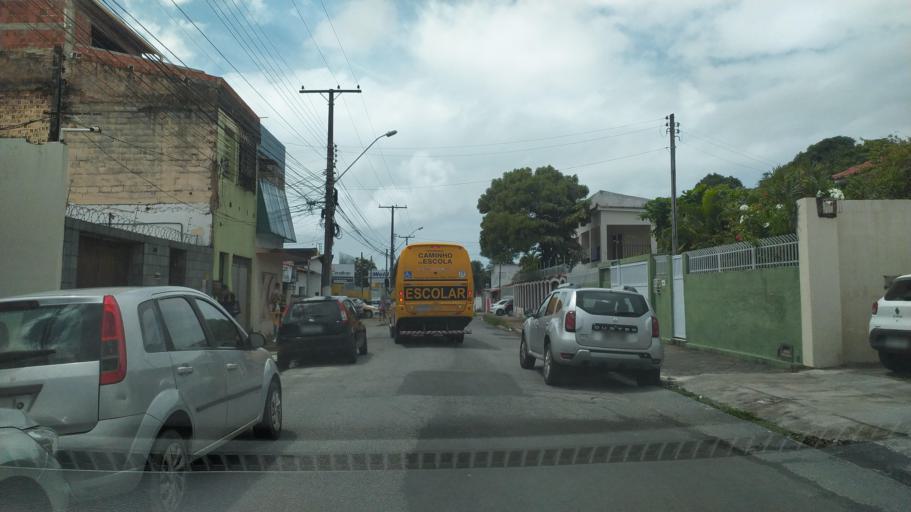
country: BR
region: Alagoas
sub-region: Maceio
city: Maceio
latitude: -9.6479
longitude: -35.7328
